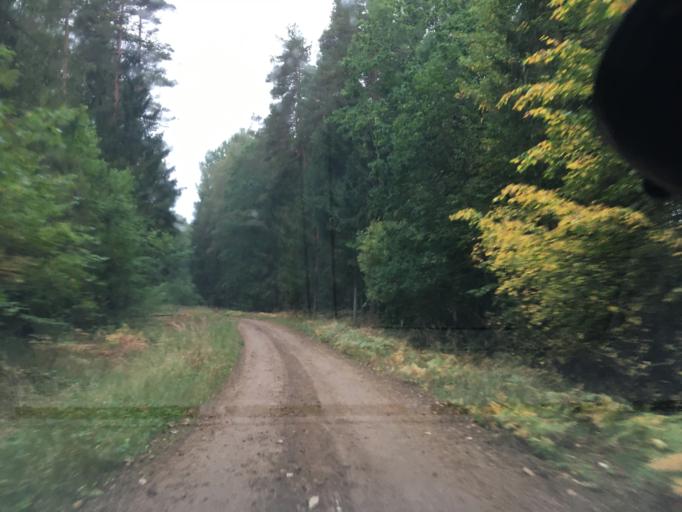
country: LV
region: Kuldigas Rajons
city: Kuldiga
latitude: 56.9874
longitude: 22.0089
